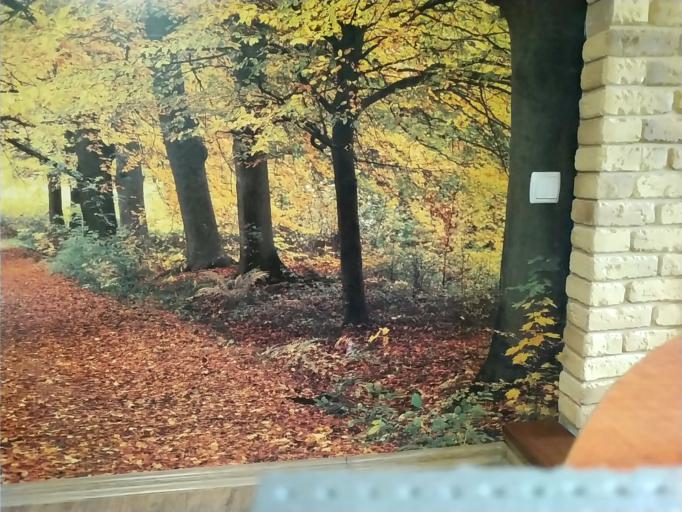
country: RU
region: Tverskaya
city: Staritsa
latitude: 56.5379
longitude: 34.9849
